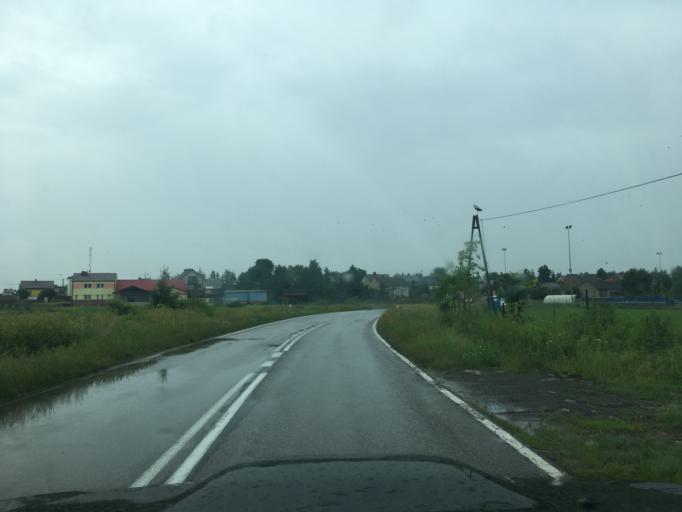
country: PL
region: Masovian Voivodeship
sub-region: Powiat otwocki
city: Sobienie Jeziory
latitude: 51.9813
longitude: 21.2809
